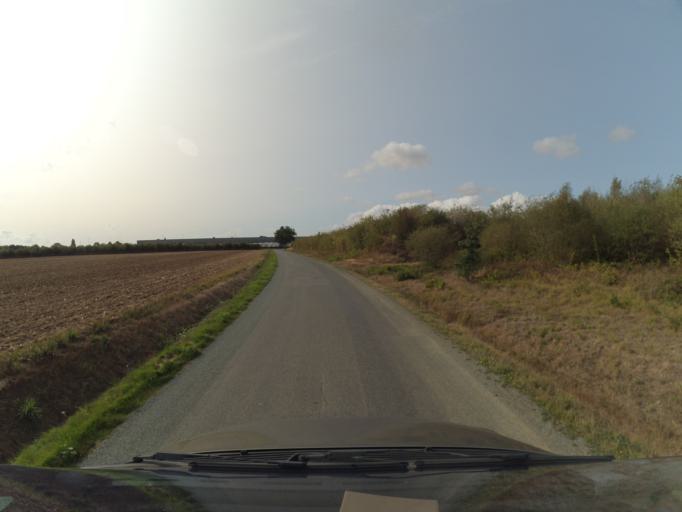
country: FR
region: Pays de la Loire
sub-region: Departement de la Vendee
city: Bouffere
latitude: 46.9453
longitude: -1.3441
